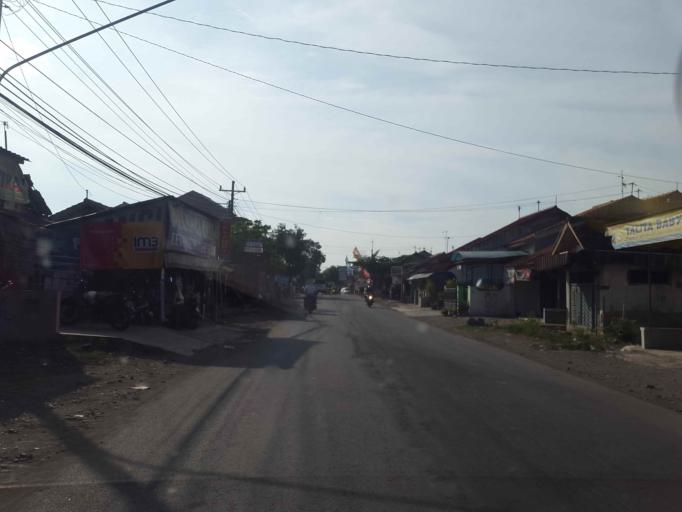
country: ID
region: Central Java
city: Tarub
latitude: -6.9481
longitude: 109.1834
